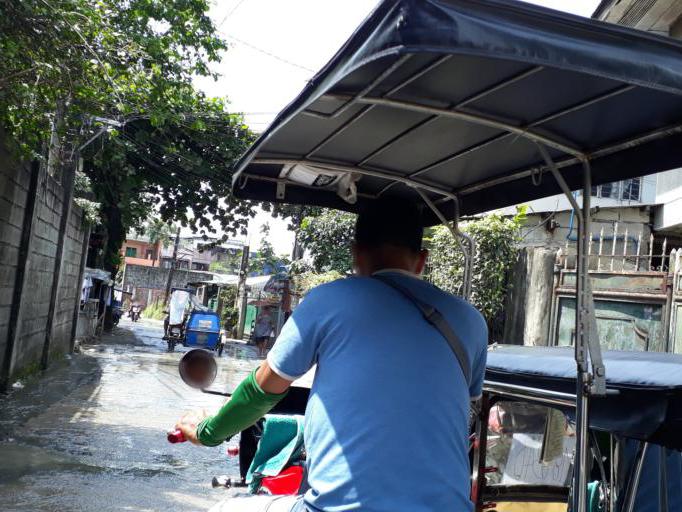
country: PH
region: Calabarzon
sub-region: Province of Rizal
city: Valenzuela
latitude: 14.6735
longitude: 120.9893
